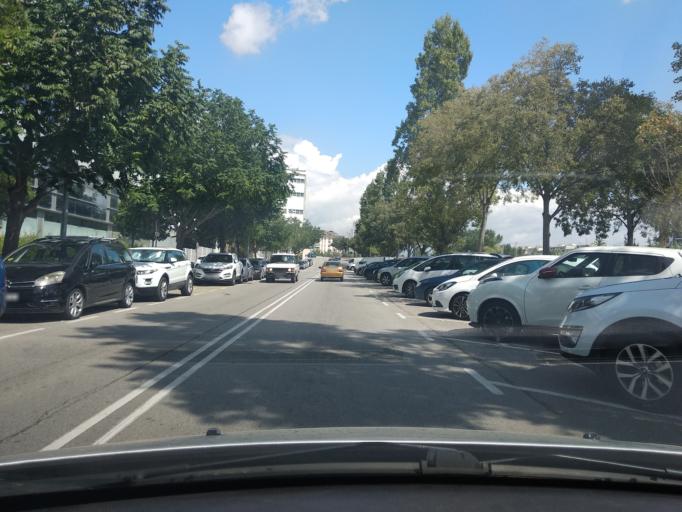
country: ES
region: Catalonia
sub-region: Provincia de Barcelona
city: Granollers
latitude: 41.6094
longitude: 2.2811
